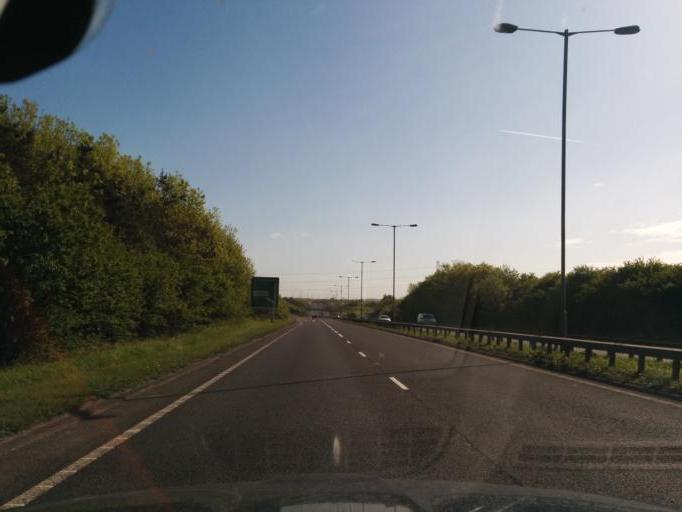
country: GB
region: England
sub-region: Northumberland
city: Ashington
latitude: 55.1521
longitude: -1.5462
